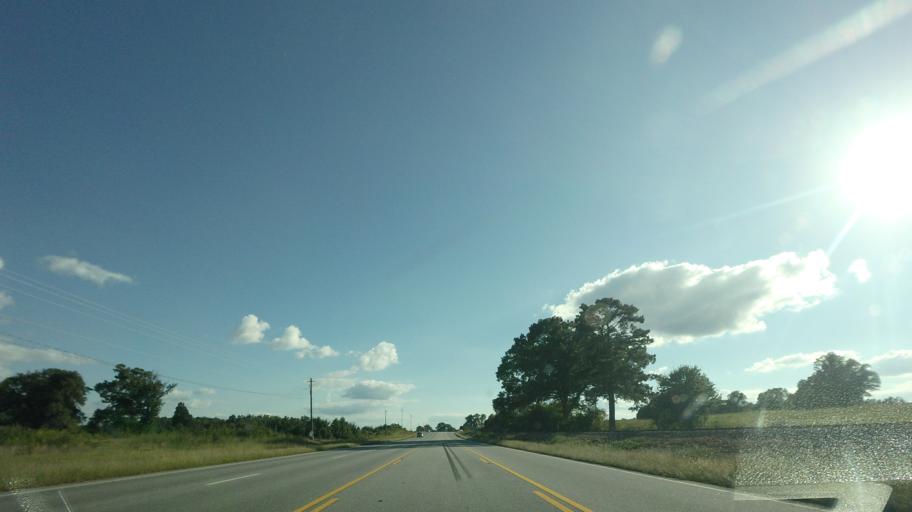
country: US
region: Georgia
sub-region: Upson County
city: Thomaston
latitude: 32.9492
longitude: -84.2543
